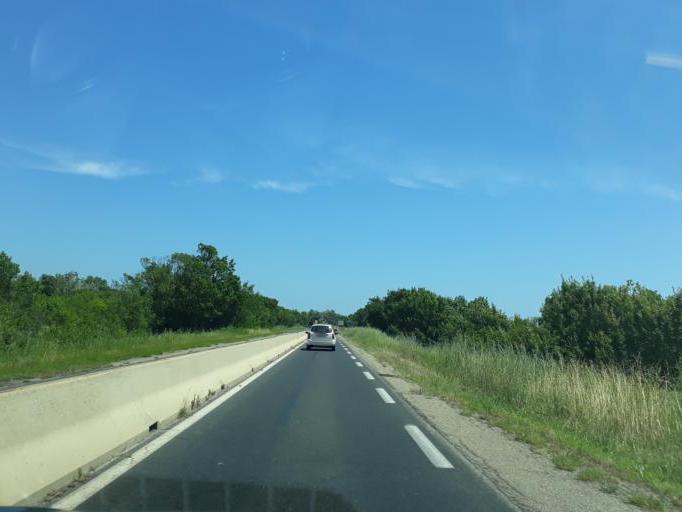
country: FR
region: Languedoc-Roussillon
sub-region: Departement de l'Herault
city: Vias
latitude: 43.3077
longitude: 3.4100
